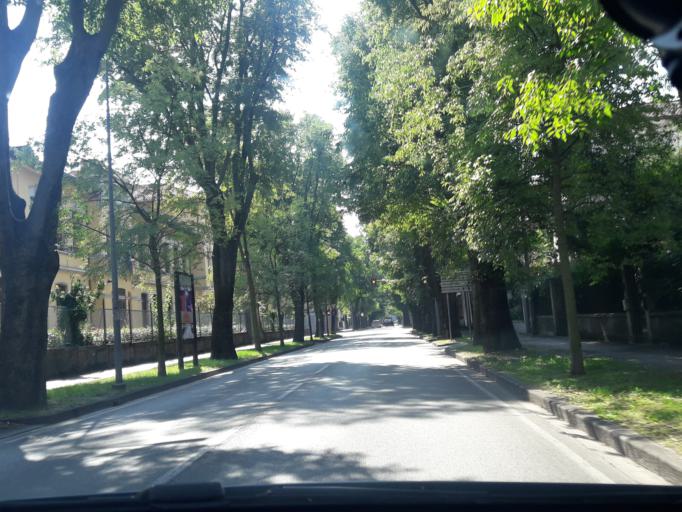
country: IT
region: Friuli Venezia Giulia
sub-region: Provincia di Udine
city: Udine
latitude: 46.0724
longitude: 13.2392
